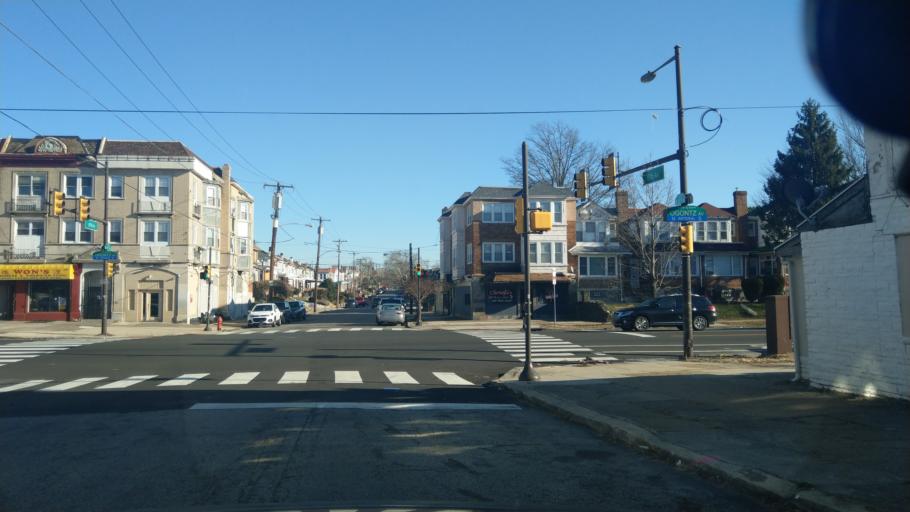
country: US
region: Pennsylvania
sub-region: Montgomery County
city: Wyncote
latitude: 40.0562
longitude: -75.1499
